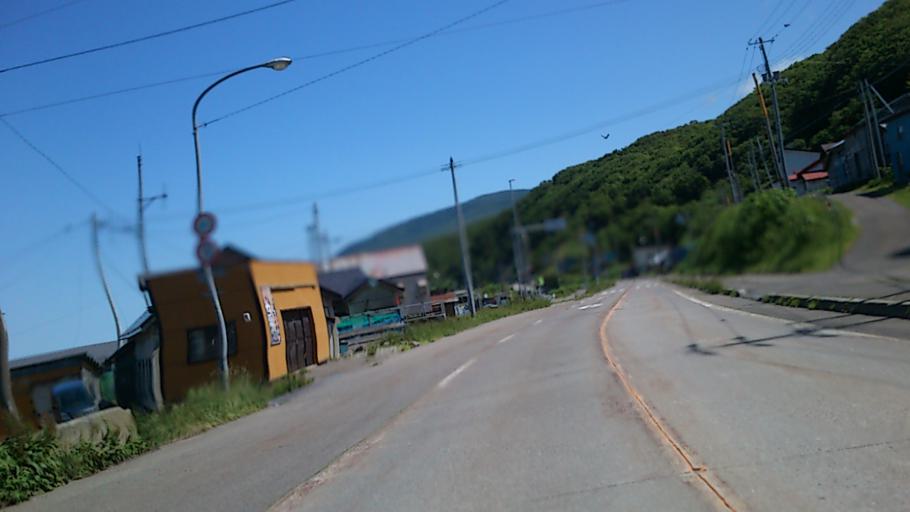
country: JP
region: Hokkaido
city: Rumoi
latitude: 43.7398
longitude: 141.3396
